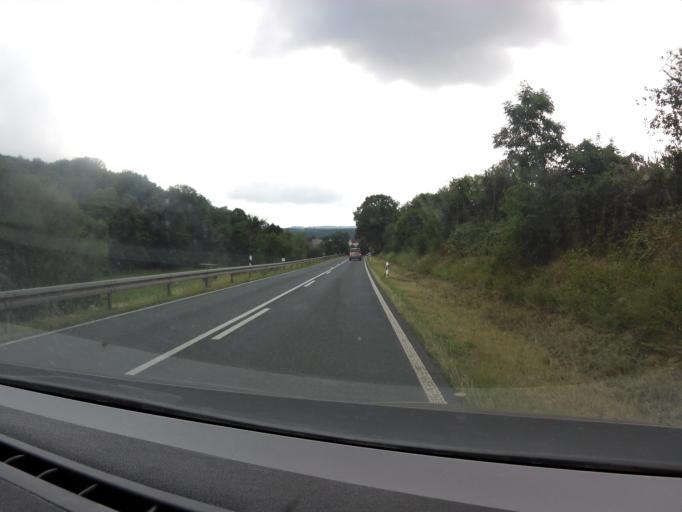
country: DE
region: Thuringia
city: Martinroda
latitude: 50.7324
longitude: 10.8886
